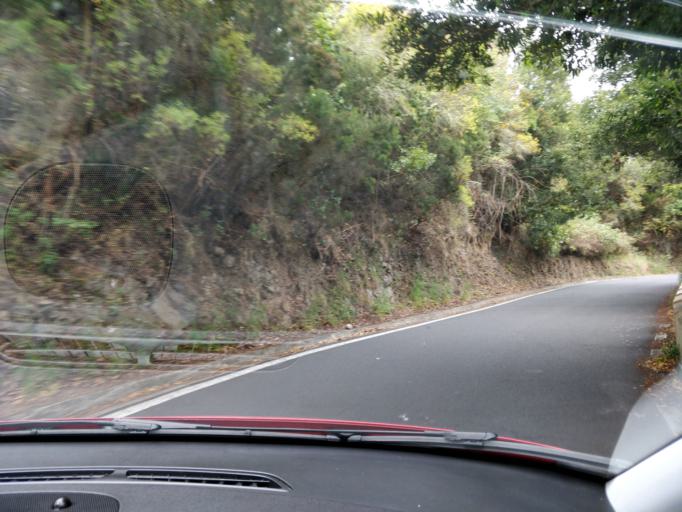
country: ES
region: Canary Islands
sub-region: Provincia de Santa Cruz de Tenerife
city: Santiago del Teide
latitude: 28.3235
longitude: -16.8426
